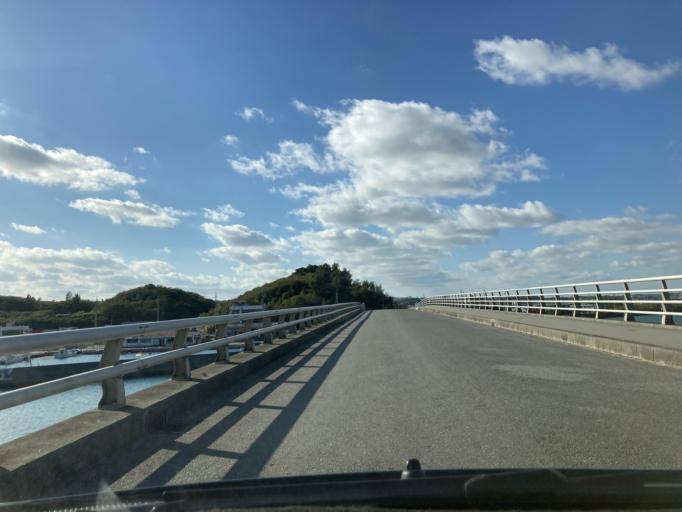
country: JP
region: Okinawa
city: Katsuren-haebaru
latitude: 26.3213
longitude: 127.9174
